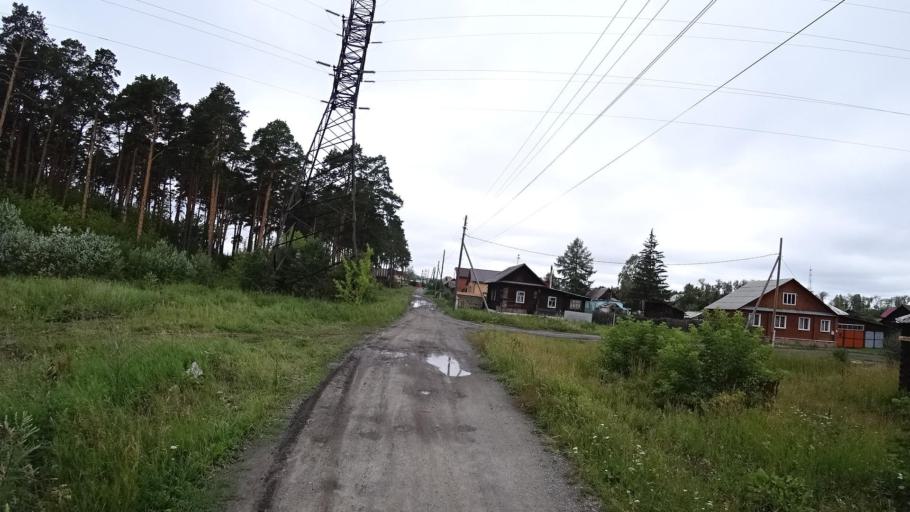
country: RU
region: Sverdlovsk
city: Kamyshlov
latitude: 56.8427
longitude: 62.7499
